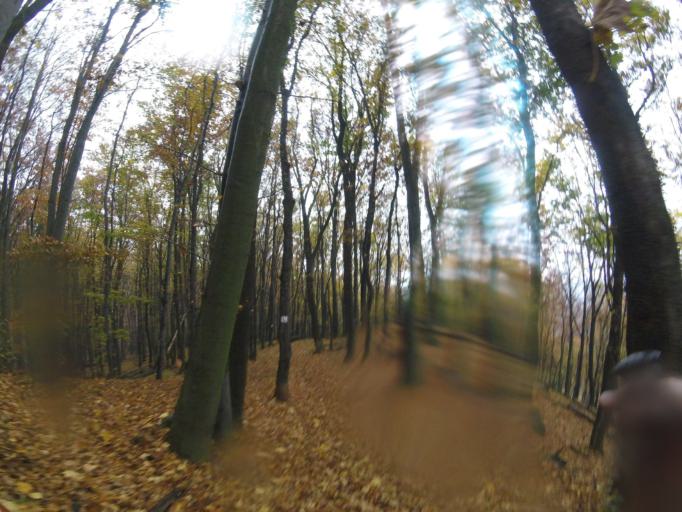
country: HU
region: Borsod-Abauj-Zemplen
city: Gonc
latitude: 48.4562
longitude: 21.3264
